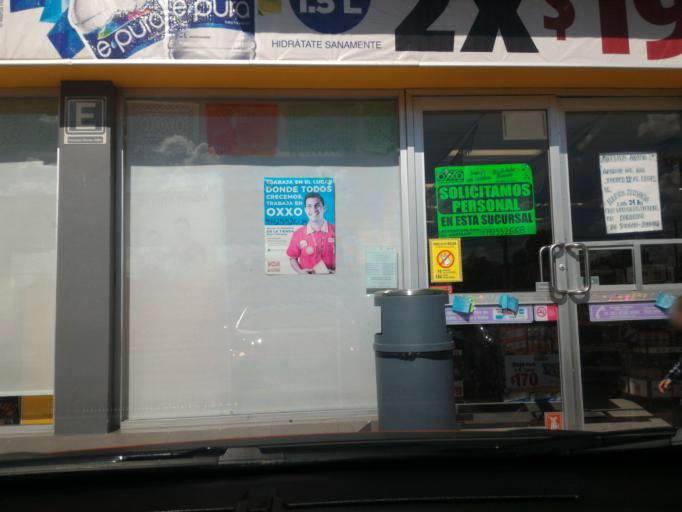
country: MX
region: Guanajuato
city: Ciudad Manuel Doblado
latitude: 20.7381
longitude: -101.9532
